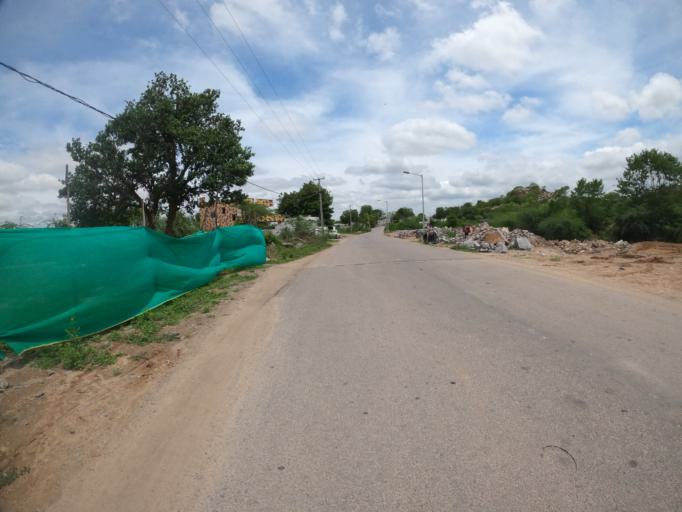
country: IN
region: Telangana
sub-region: Hyderabad
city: Hyderabad
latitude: 17.2969
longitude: 78.3792
